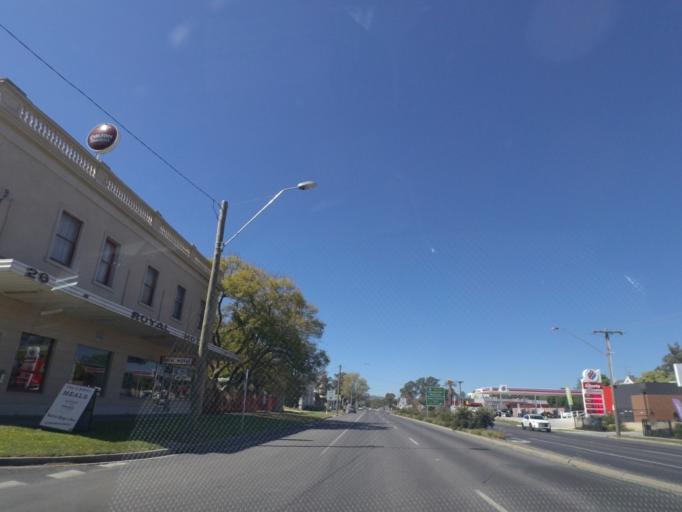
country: AU
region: Victoria
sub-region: Murrindindi
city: Kinglake West
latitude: -37.0204
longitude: 145.1268
